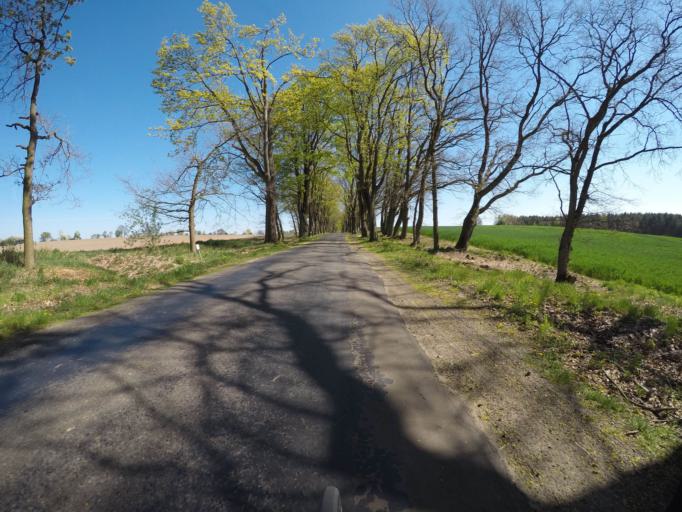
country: DE
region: Brandenburg
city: Strausberg
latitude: 52.6190
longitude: 13.8439
